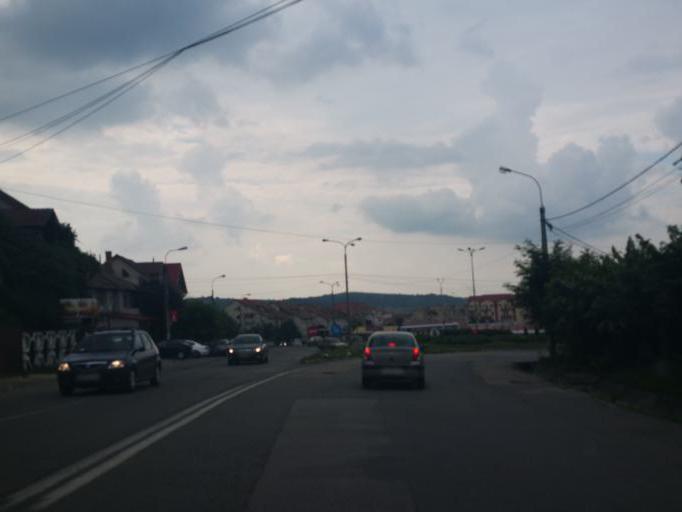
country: RO
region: Salaj
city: Zalau
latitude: 47.1678
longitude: 23.0730
